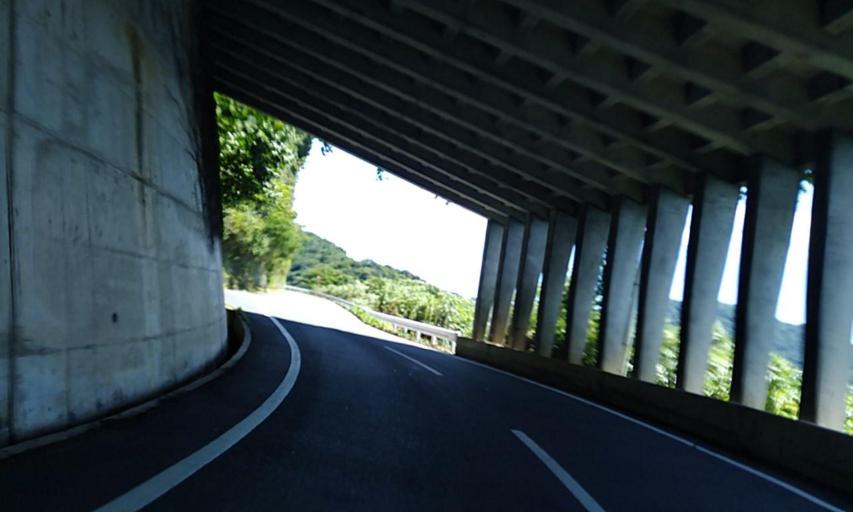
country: JP
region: Kyoto
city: Miyazu
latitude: 35.6672
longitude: 135.2738
